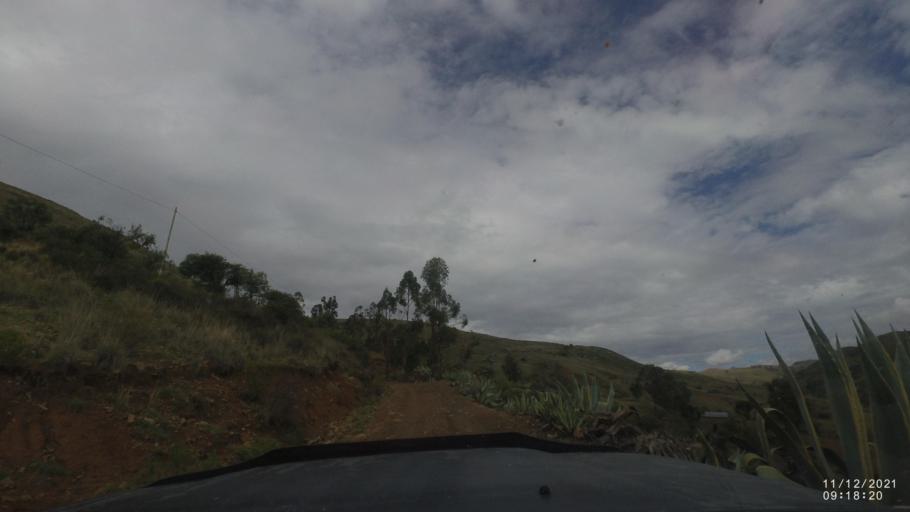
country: BO
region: Cochabamba
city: Tarata
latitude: -17.8817
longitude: -65.9676
